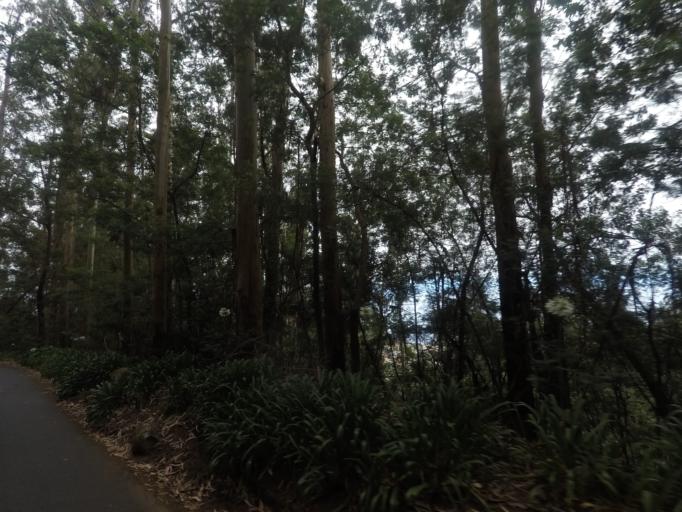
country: PT
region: Madeira
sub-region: Funchal
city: Nossa Senhora do Monte
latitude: 32.6665
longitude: -16.8762
